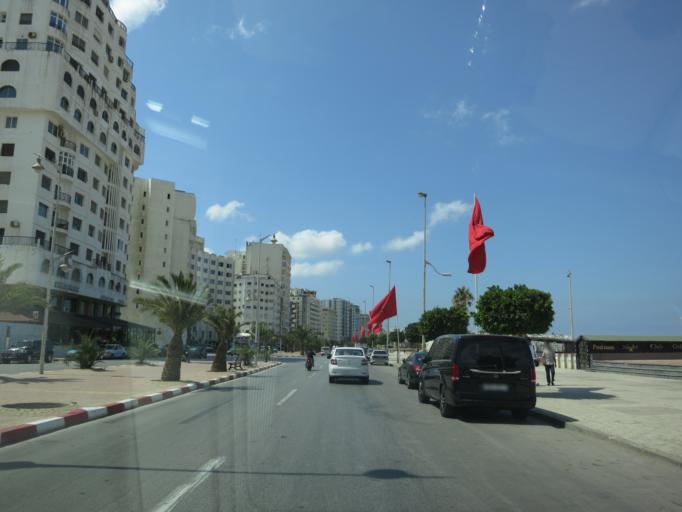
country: MA
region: Tanger-Tetouan
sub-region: Tanger-Assilah
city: Tangier
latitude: 35.7766
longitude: -5.7961
